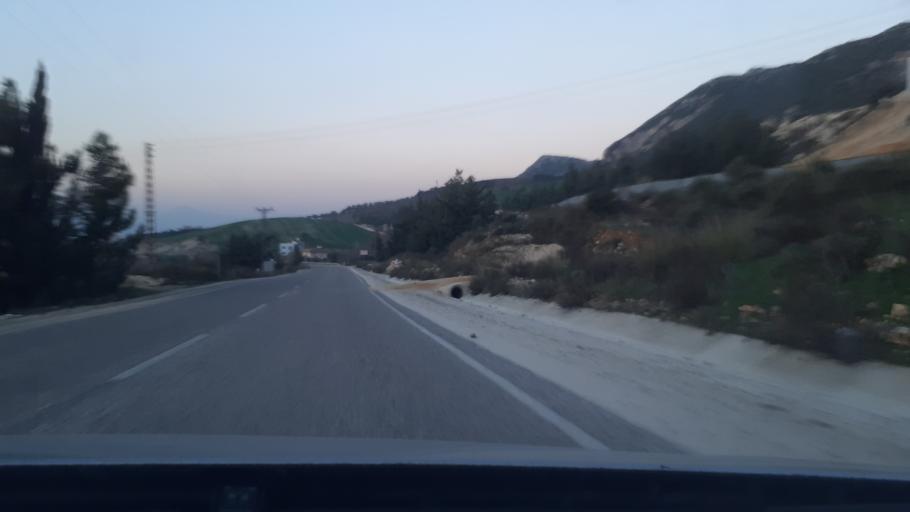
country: TR
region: Hatay
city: Dursunlu
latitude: 36.1767
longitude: 36.1883
